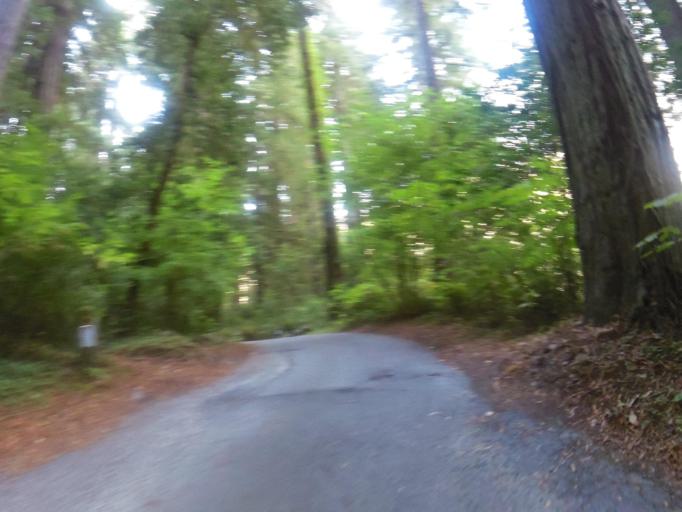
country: US
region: California
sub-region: Del Norte County
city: Bertsch-Oceanview
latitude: 41.8017
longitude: -124.0861
